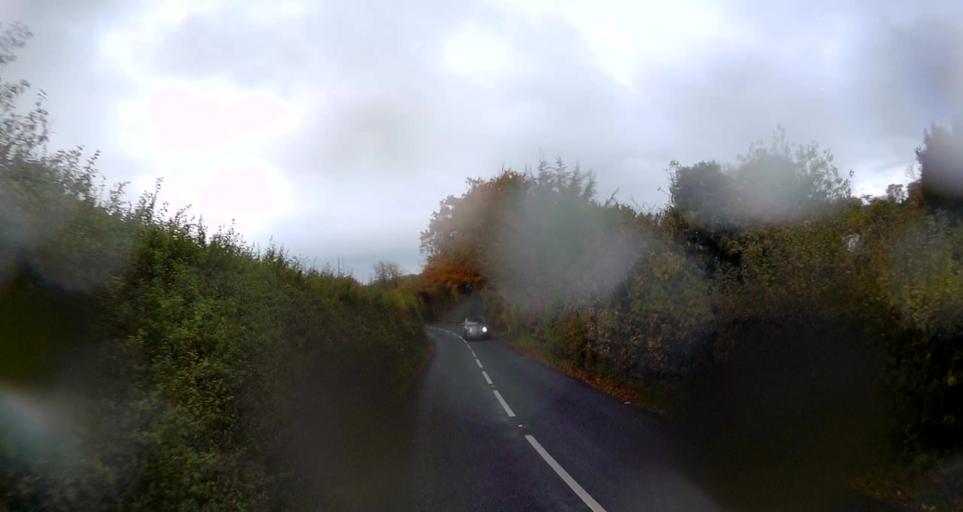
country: GB
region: England
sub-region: Hampshire
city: Kings Worthy
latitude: 51.1340
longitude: -1.1876
